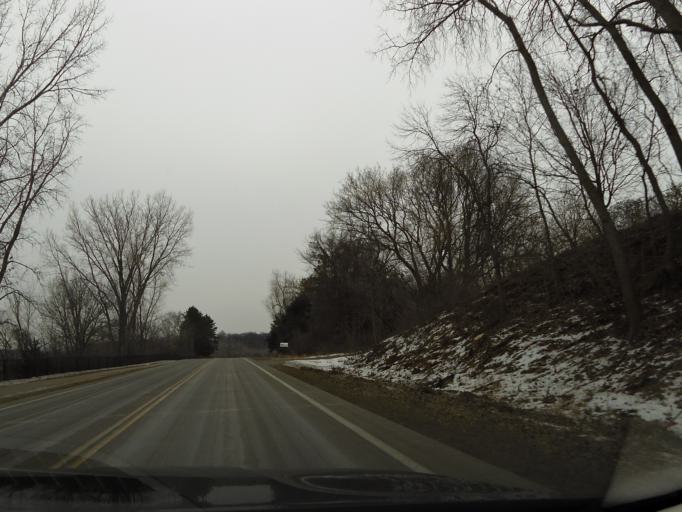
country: US
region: Minnesota
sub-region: Scott County
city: Jordan
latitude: 44.6549
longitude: -93.6334
